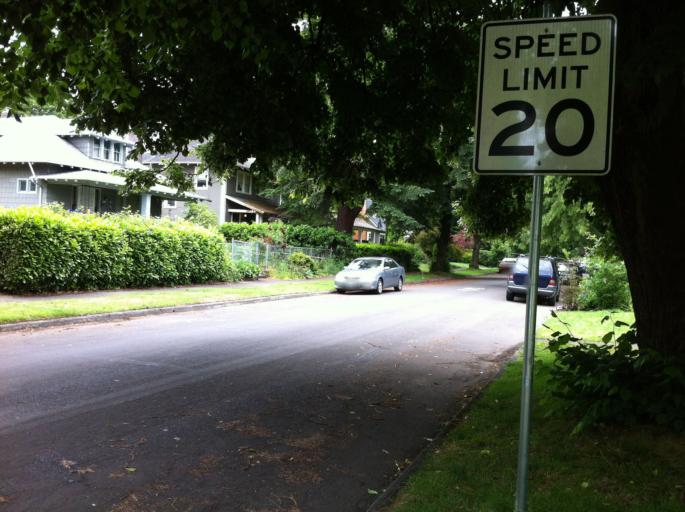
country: US
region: Oregon
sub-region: Multnomah County
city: Portland
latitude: 45.5663
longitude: -122.6670
